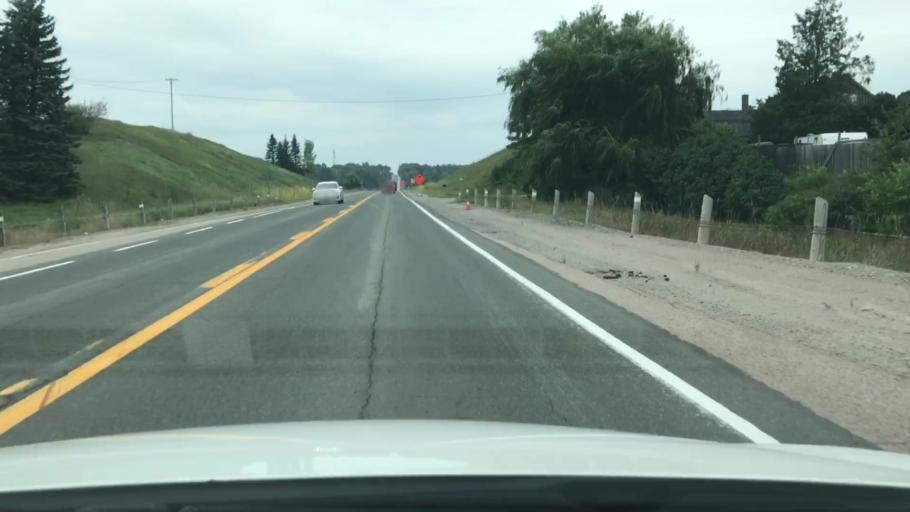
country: CA
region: Ontario
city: Innisfil
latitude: 44.2396
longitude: -79.5979
